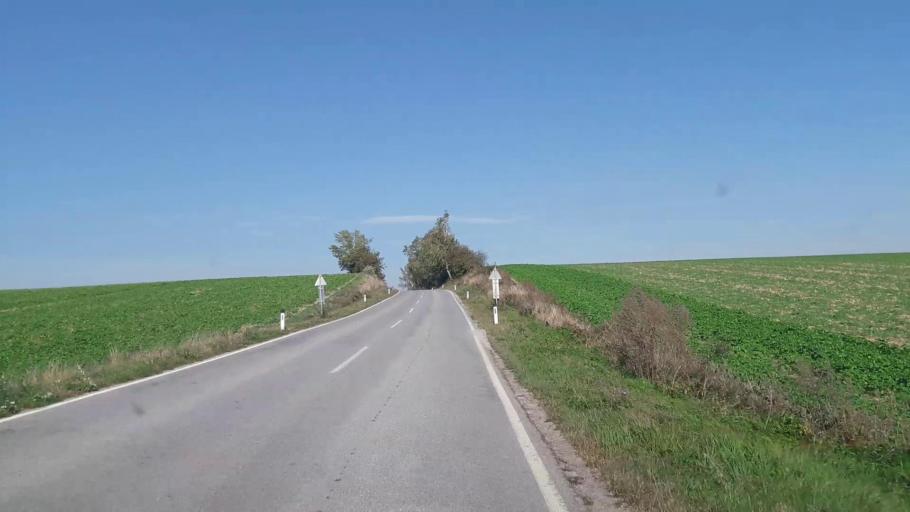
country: AT
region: Lower Austria
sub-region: Politischer Bezirk Korneuburg
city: Ernstbrunn
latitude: 48.5139
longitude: 16.3599
